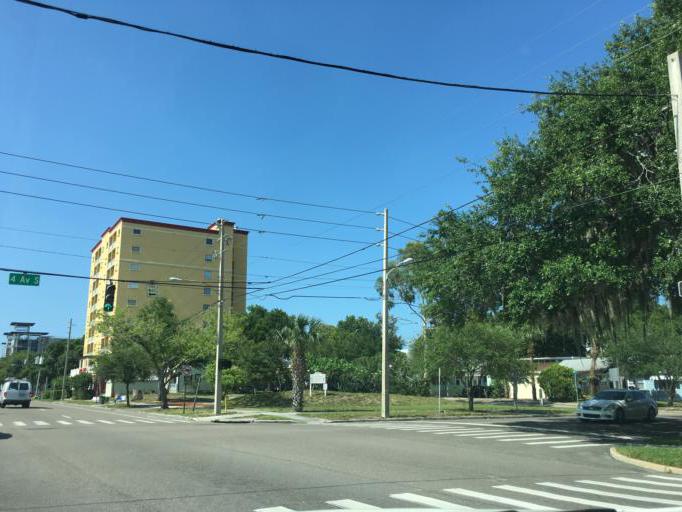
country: US
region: Florida
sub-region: Pinellas County
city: Saint Petersburg
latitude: 27.7669
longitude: -82.6448
